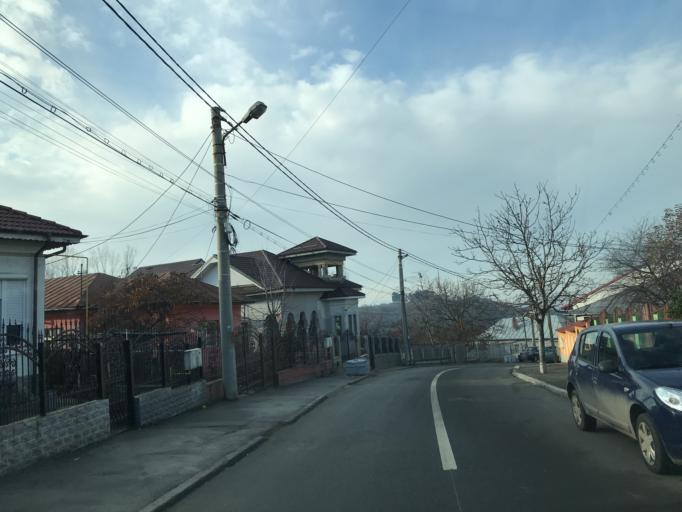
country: RO
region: Olt
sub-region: Municipiul Slatina
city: Slatina
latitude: 44.4259
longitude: 24.3599
